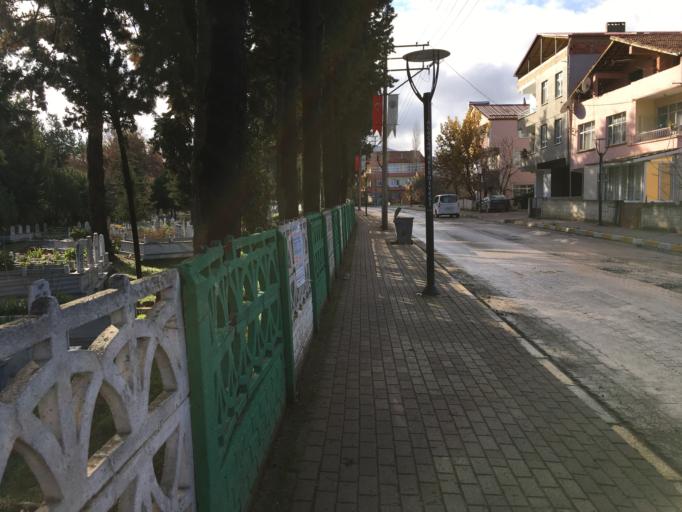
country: TR
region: Samsun
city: Alacam
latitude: 41.6154
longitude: 35.6034
